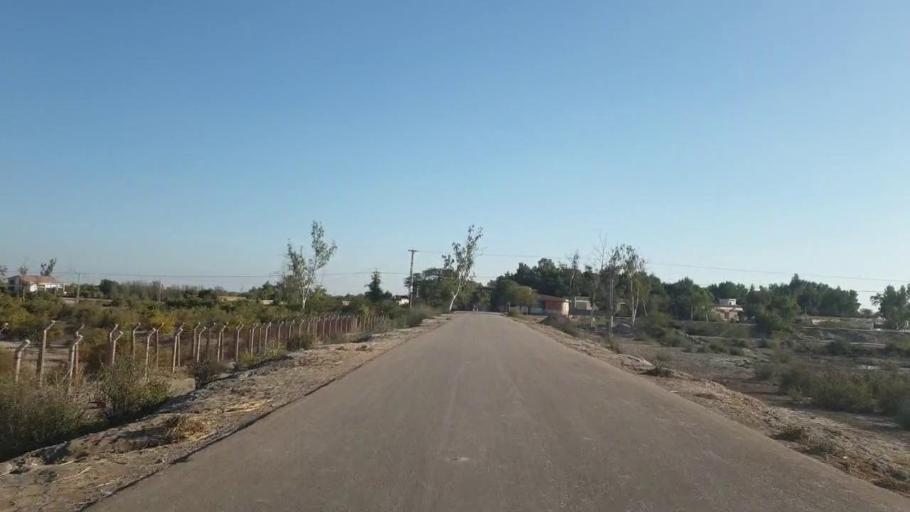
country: PK
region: Sindh
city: Dokri
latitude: 27.3312
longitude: 68.1309
